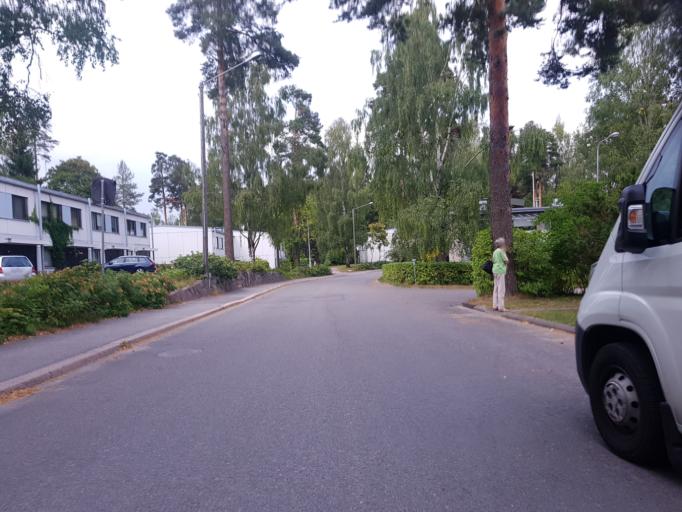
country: FI
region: Uusimaa
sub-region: Helsinki
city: Helsinki
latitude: 60.2254
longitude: 24.9464
